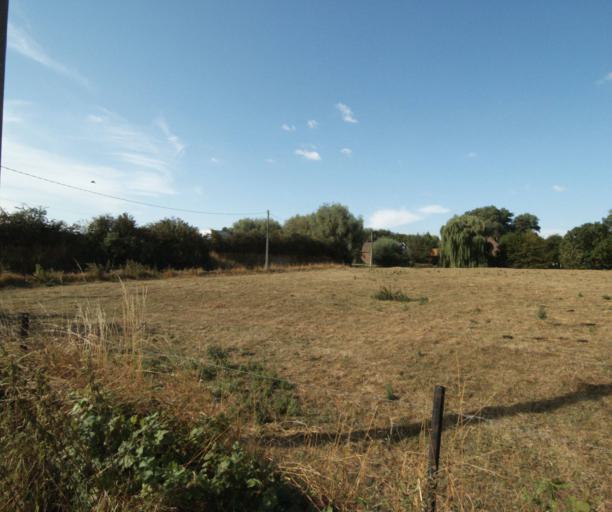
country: FR
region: Nord-Pas-de-Calais
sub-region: Departement du Nord
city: Roncq
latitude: 50.7562
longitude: 3.1319
